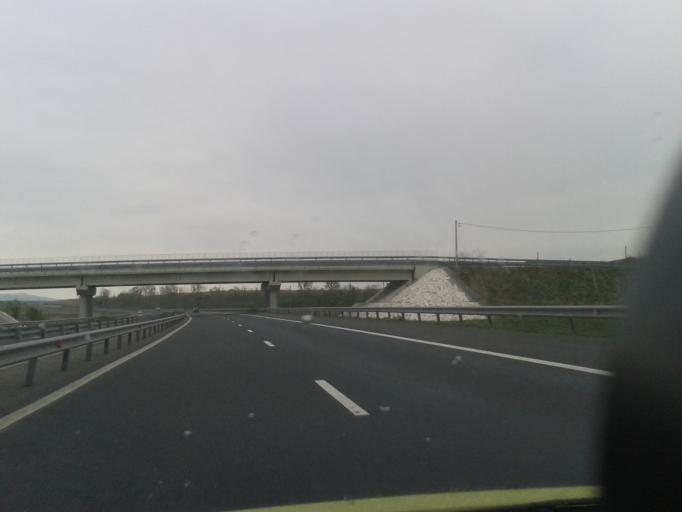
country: RO
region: Hunedoara
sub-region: Comuna Turdas
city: Turdas
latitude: 45.8384
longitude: 23.1173
